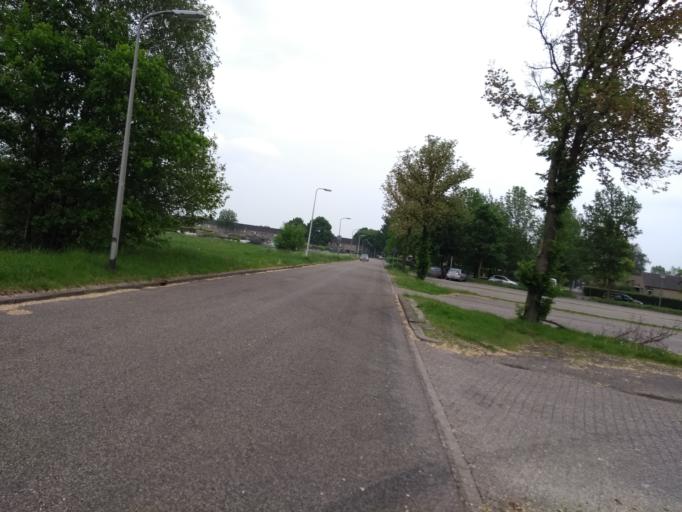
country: NL
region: Overijssel
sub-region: Gemeente Almelo
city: Almelo
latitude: 52.3848
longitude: 6.6726
